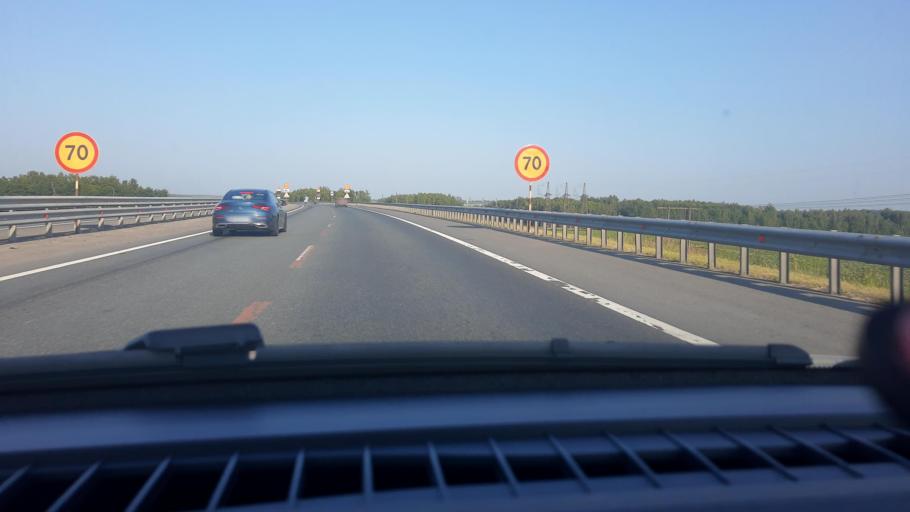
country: RU
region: Nizjnij Novgorod
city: Burevestnik
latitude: 56.1148
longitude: 43.8268
